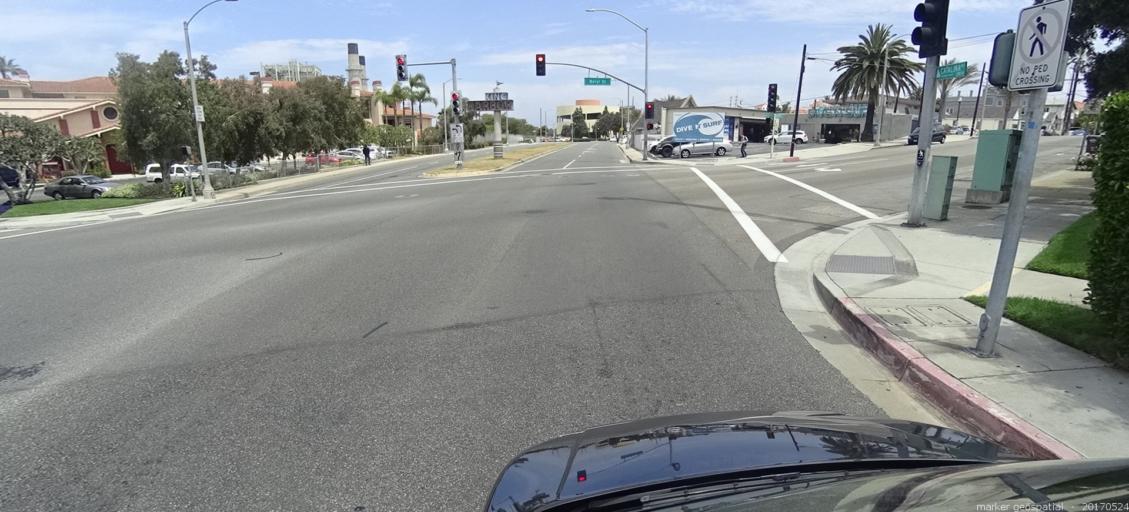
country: US
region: California
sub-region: Los Angeles County
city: Redondo Beach
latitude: 33.8464
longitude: -118.3919
